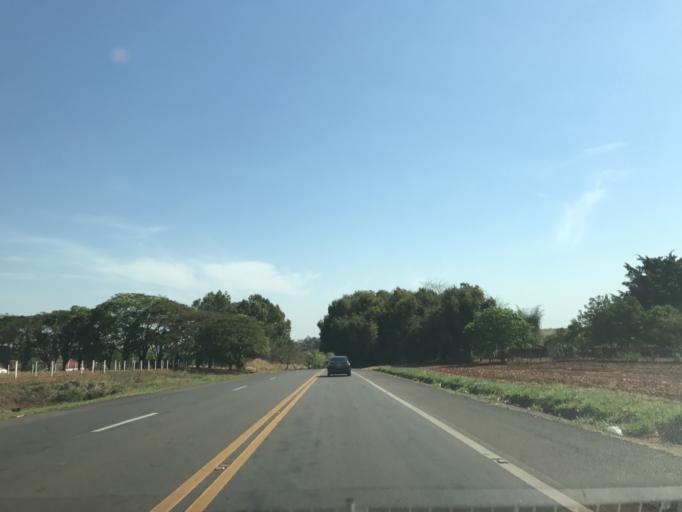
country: BR
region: Sao Paulo
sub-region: Jose Bonifacio
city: Jose Bonifacio
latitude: -21.0144
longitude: -49.6510
